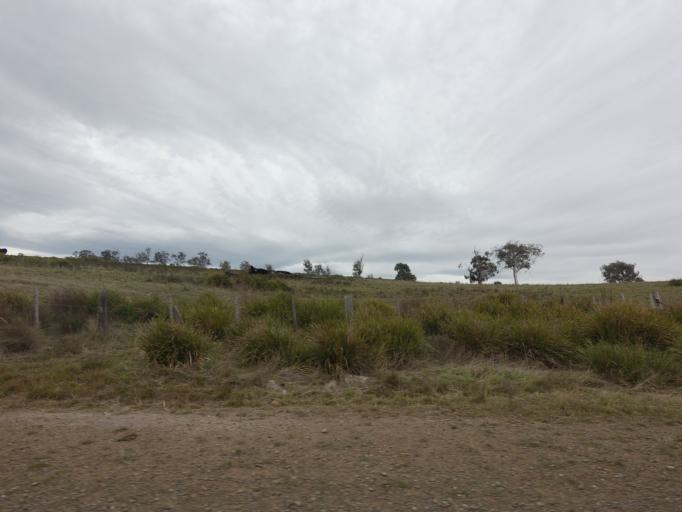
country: AU
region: Tasmania
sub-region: Derwent Valley
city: New Norfolk
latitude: -42.3949
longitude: 146.8821
